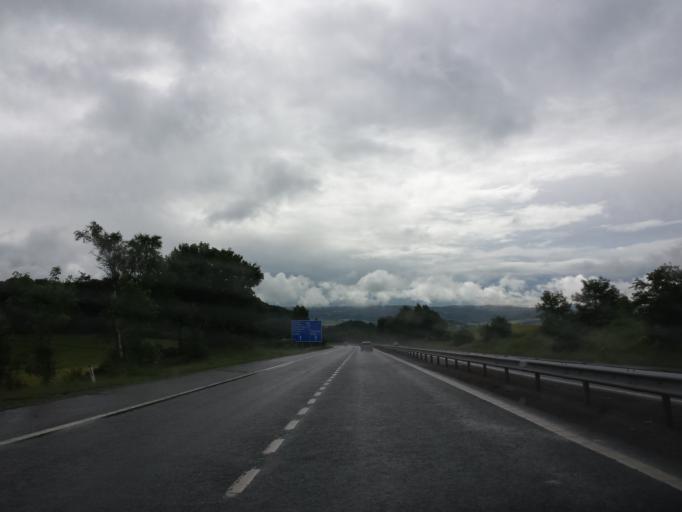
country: GB
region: Scotland
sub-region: Perth and Kinross
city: Perth
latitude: 56.3709
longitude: -3.4382
